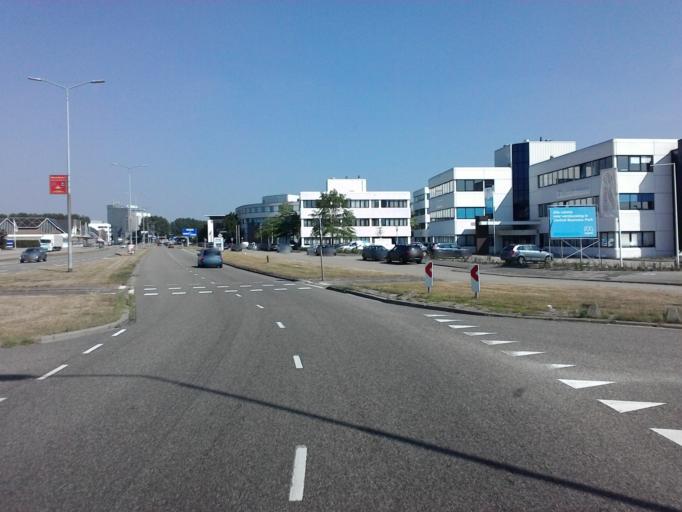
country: NL
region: Utrecht
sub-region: Stichtse Vecht
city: Maarssen
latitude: 52.1165
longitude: 5.0480
